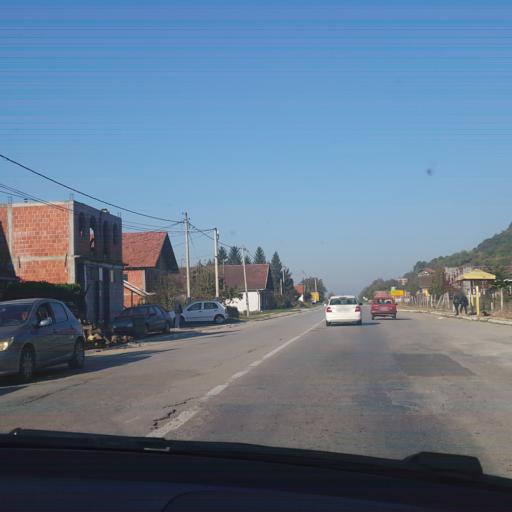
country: RS
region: Central Serbia
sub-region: Toplicki Okrug
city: Prokuplje
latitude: 43.2316
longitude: 21.5536
